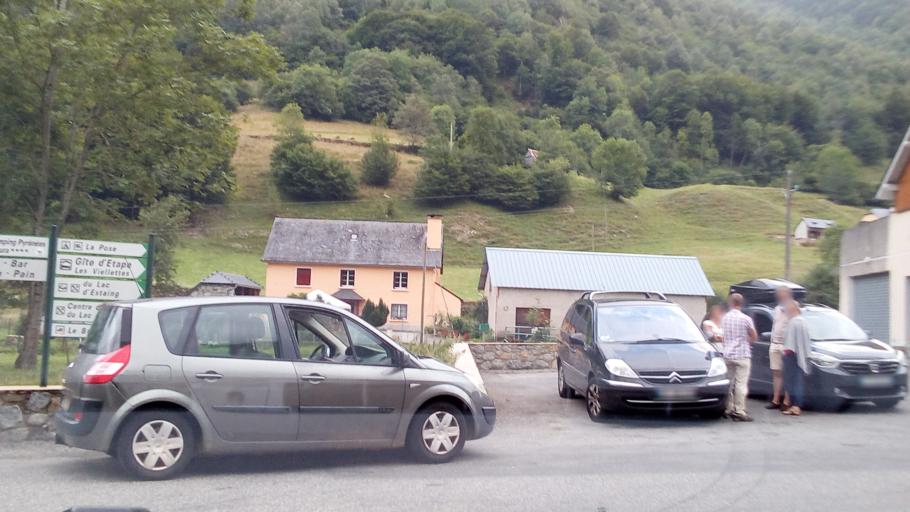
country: FR
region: Midi-Pyrenees
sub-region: Departement des Hautes-Pyrenees
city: Cauterets
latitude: 42.9397
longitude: -0.1783
